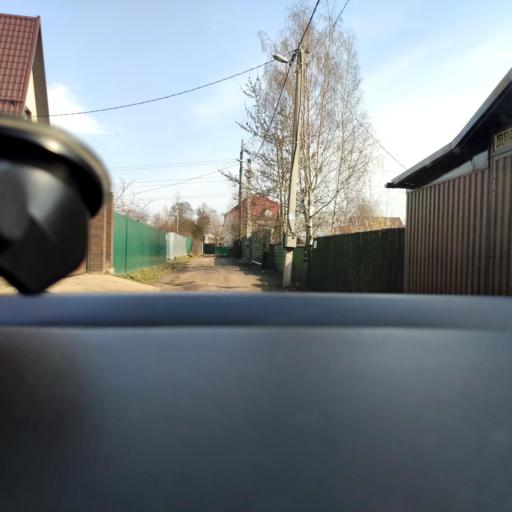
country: RU
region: Moskovskaya
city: Sheremet'yevskiy
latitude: 55.9804
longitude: 37.5195
